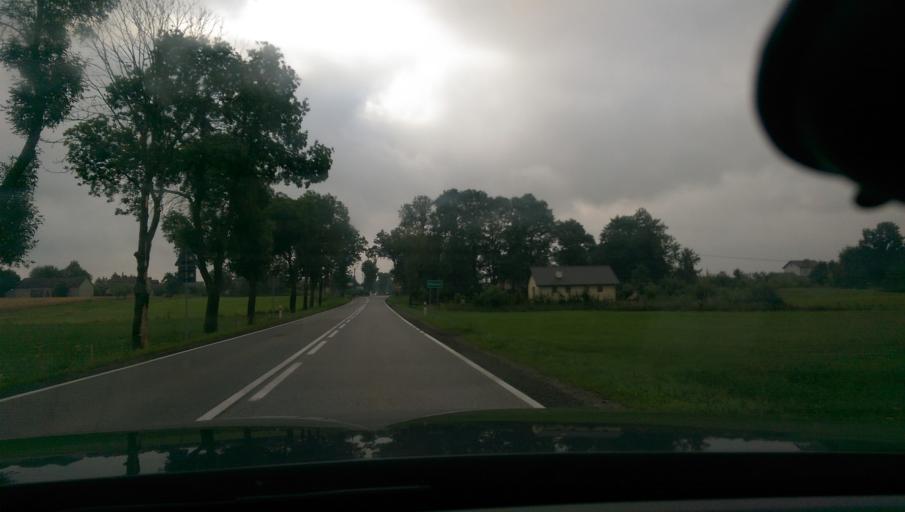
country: PL
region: Masovian Voivodeship
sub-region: Powiat przasnyski
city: Przasnysz
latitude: 53.0701
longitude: 20.8589
